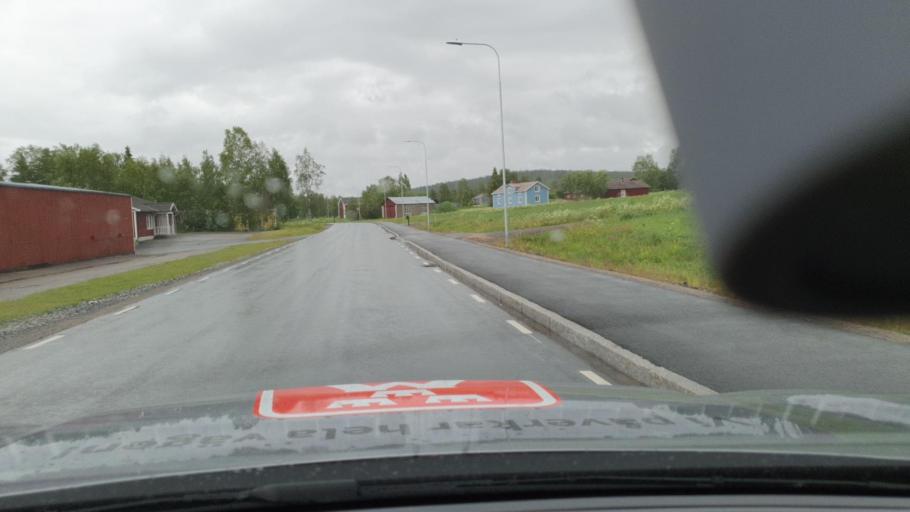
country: FI
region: Lapland
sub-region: Torniolaakso
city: Ylitornio
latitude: 66.2220
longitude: 23.6926
